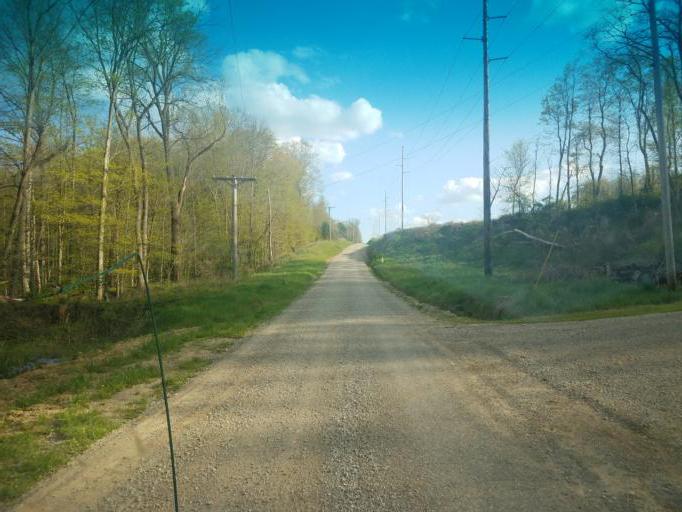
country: US
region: Ohio
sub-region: Wayne County
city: Shreve
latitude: 40.6538
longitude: -82.0336
